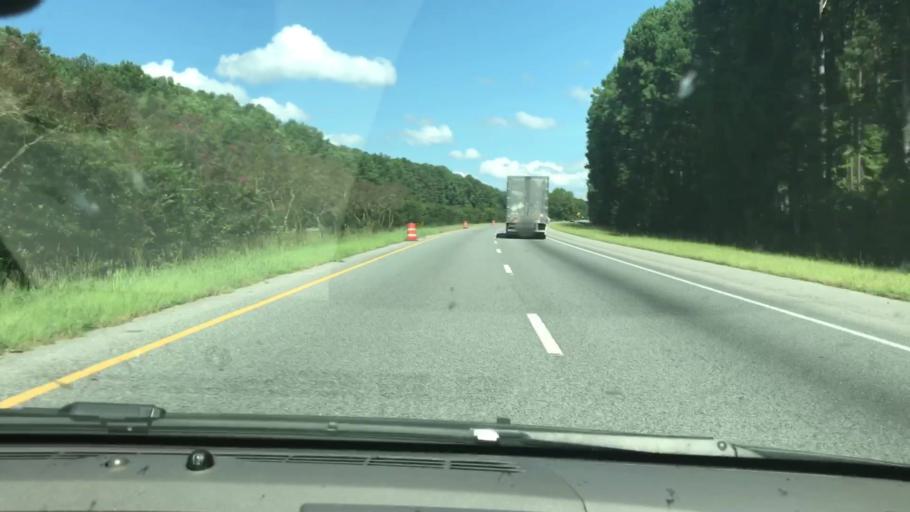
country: US
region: Georgia
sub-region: Harris County
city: Hamilton
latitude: 32.7028
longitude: -85.0078
